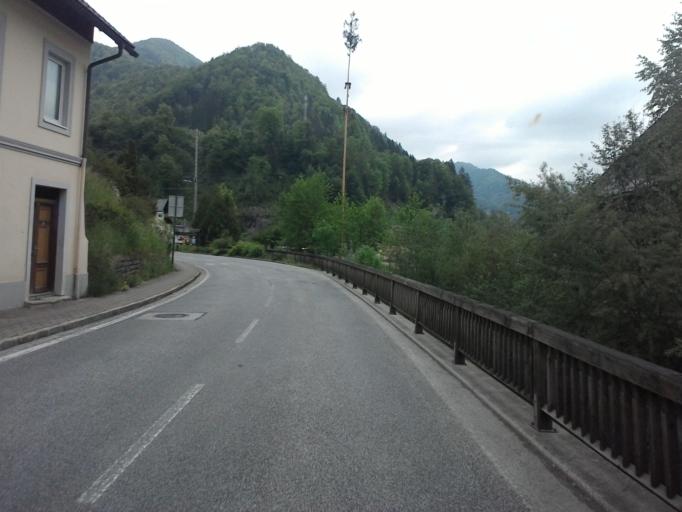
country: AT
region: Styria
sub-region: Politischer Bezirk Liezen
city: Landl
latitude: 47.6663
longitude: 14.7125
